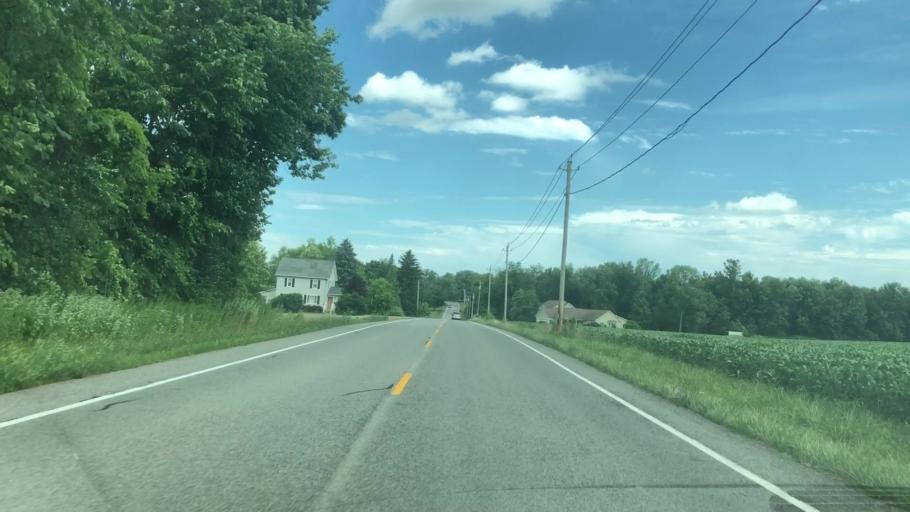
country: US
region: New York
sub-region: Wayne County
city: Macedon
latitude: 43.1177
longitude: -77.3525
